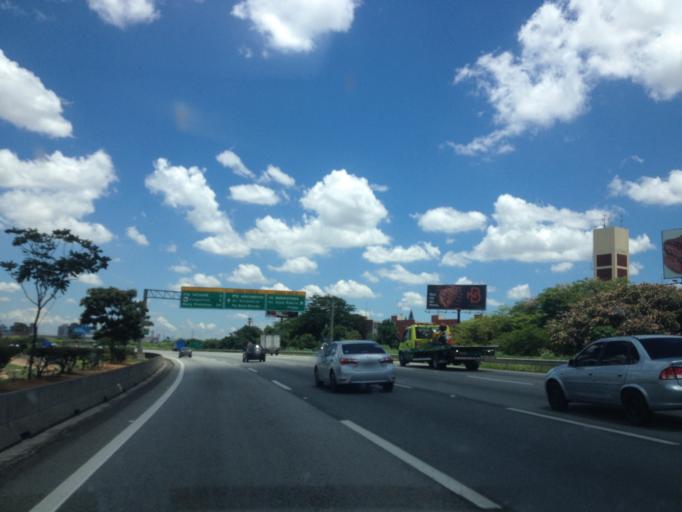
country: BR
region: Sao Paulo
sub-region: Guarulhos
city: Guarulhos
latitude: -23.5070
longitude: -46.5526
